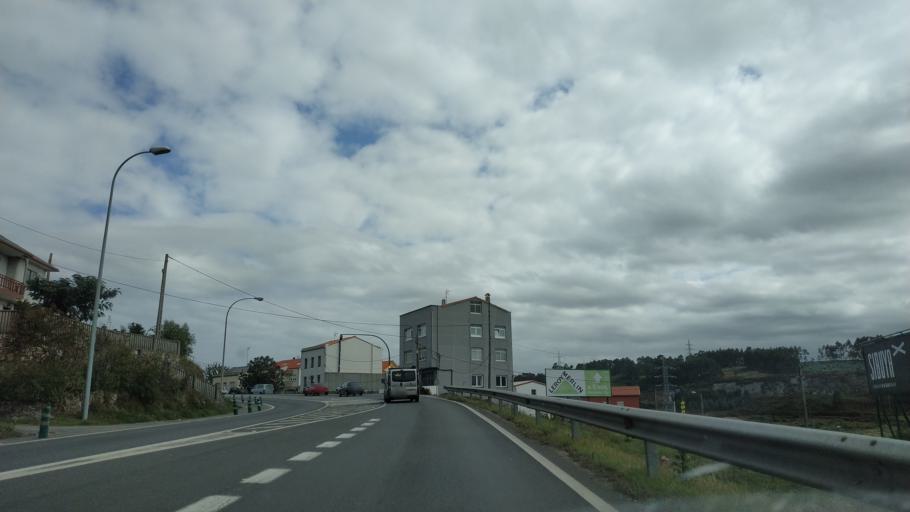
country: ES
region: Galicia
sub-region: Provincia da Coruna
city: Arteixo
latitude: 43.3282
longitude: -8.4694
